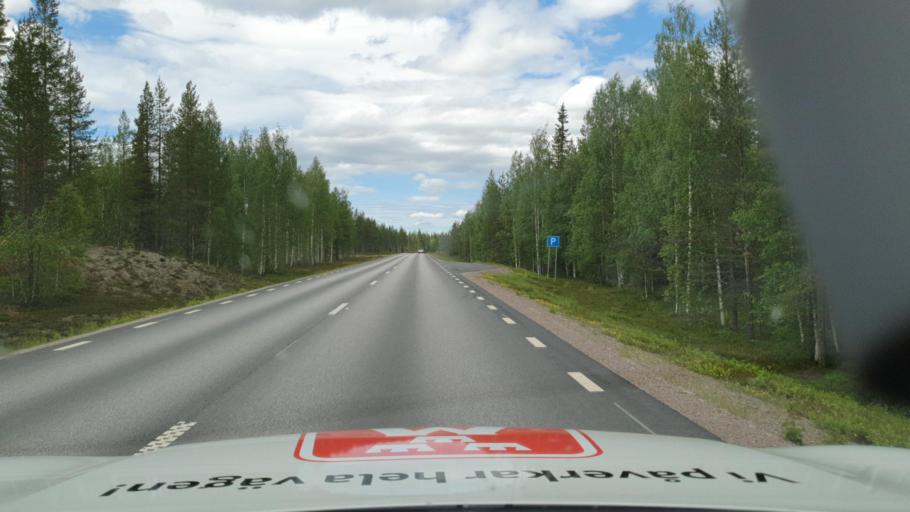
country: SE
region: Vaesterbotten
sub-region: Skelleftea Kommun
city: Langsele
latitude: 65.1400
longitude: 19.9037
